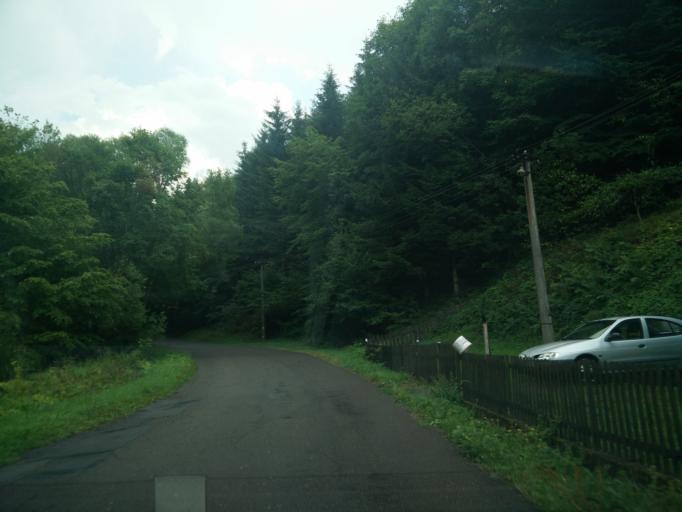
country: SK
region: Banskobystricky
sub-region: Okres Banska Bystrica
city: Banska Stiavnica
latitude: 48.4889
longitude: 18.8495
